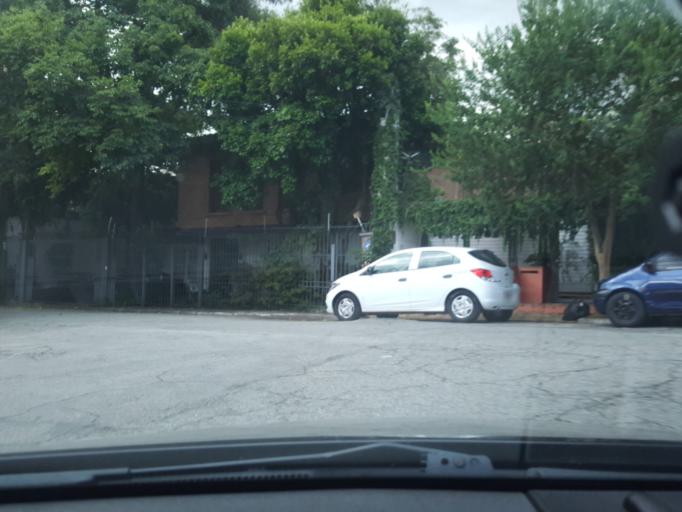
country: BR
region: Sao Paulo
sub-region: Sao Paulo
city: Sao Paulo
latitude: -23.5721
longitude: -46.6846
